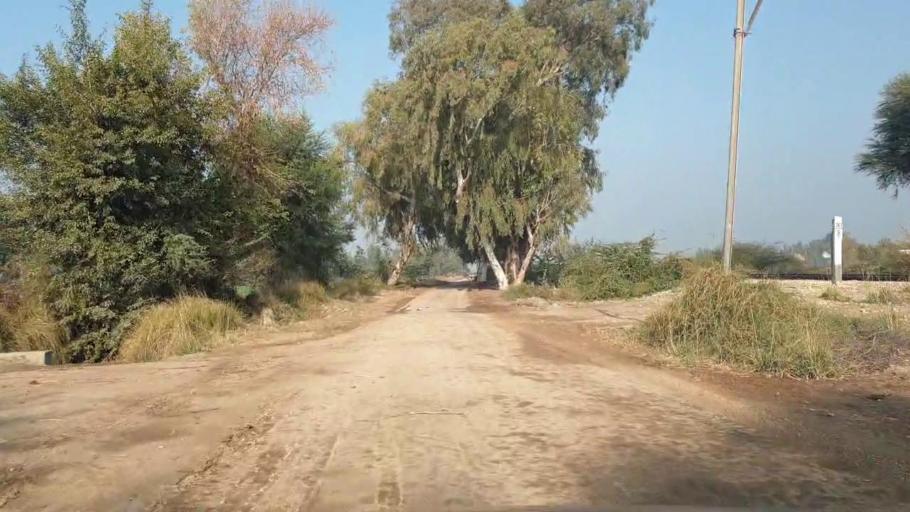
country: PK
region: Sindh
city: Shahdadpur
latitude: 25.9693
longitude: 68.6073
